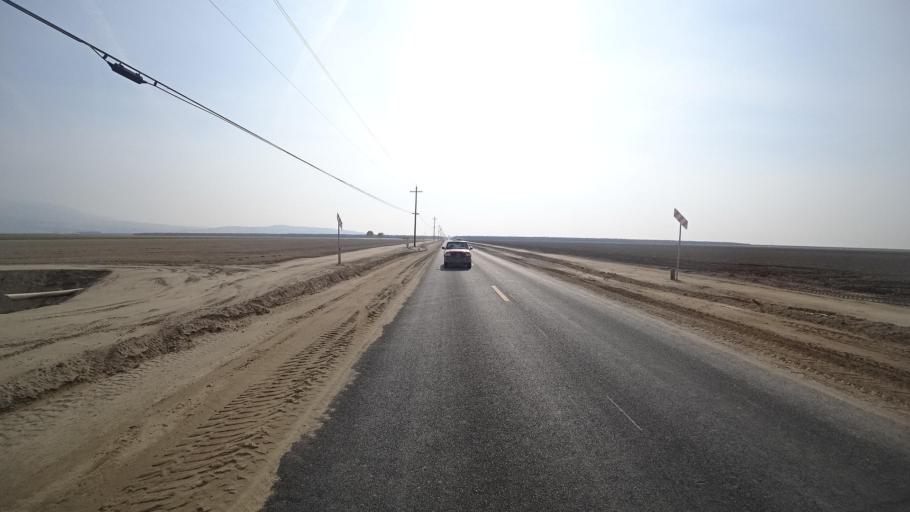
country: US
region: California
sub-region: Kern County
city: Arvin
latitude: 35.1725
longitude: -118.8510
